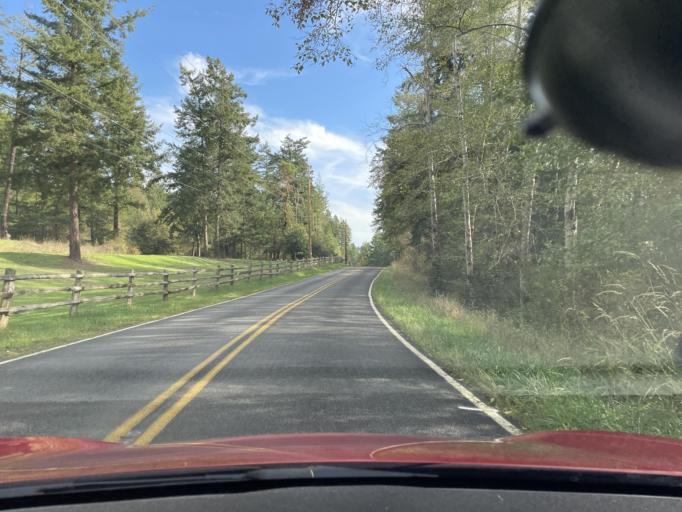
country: US
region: Washington
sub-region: San Juan County
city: Friday Harbor
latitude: 48.5186
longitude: -122.9887
